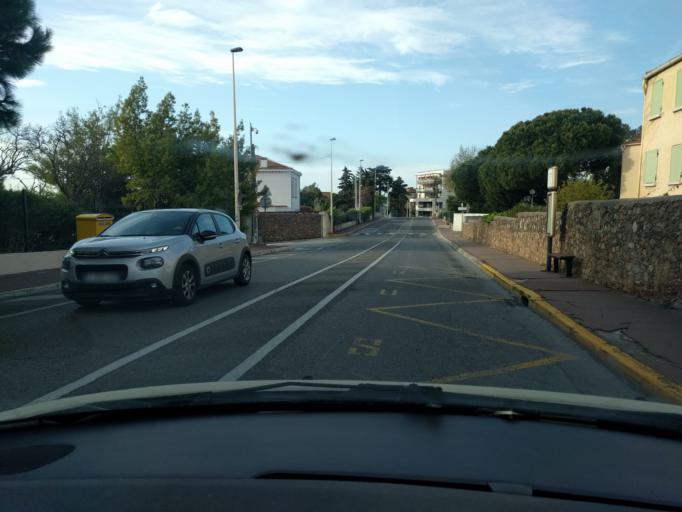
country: FR
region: Provence-Alpes-Cote d'Azur
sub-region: Departement des Alpes-Maritimes
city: Cannes
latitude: 43.5582
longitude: 6.9737
